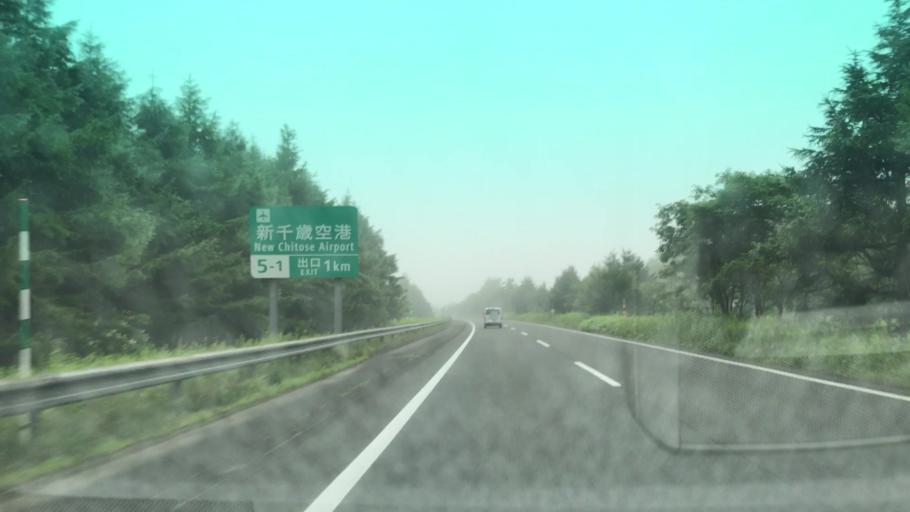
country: JP
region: Hokkaido
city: Chitose
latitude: 42.7876
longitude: 141.6265
